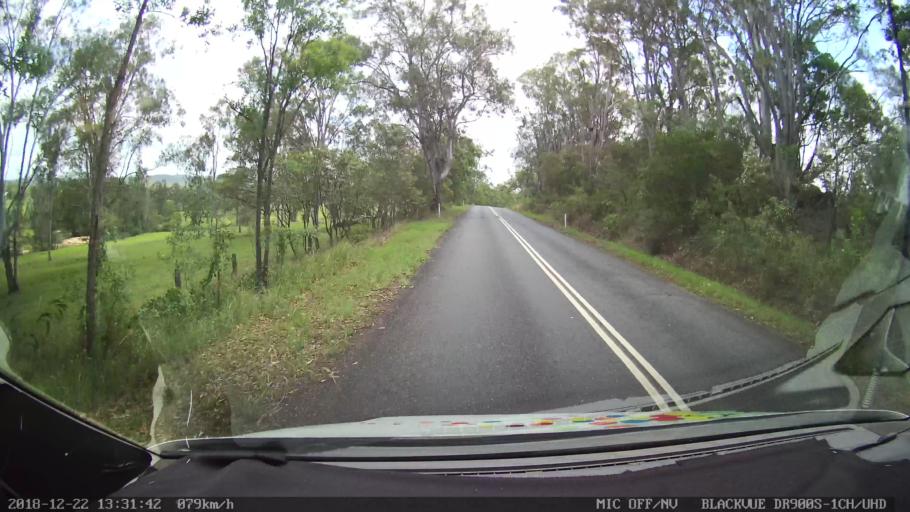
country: AU
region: New South Wales
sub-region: Clarence Valley
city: Coutts Crossing
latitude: -29.8577
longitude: 152.8501
